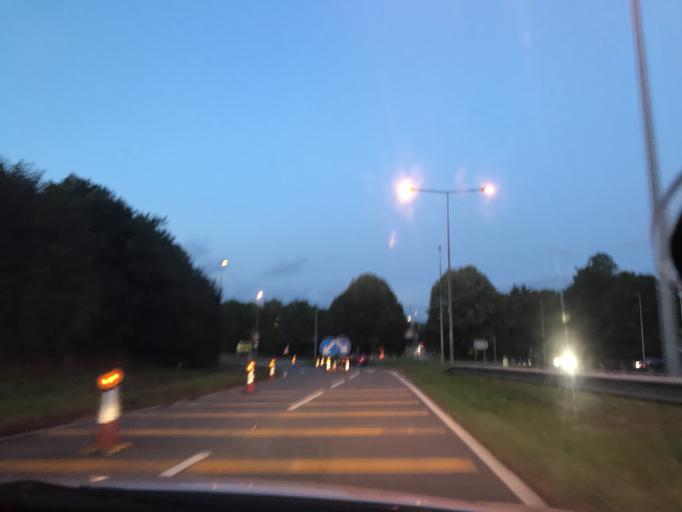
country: GB
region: England
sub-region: Cheshire West and Chester
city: Northwich
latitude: 53.2386
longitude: -2.5145
